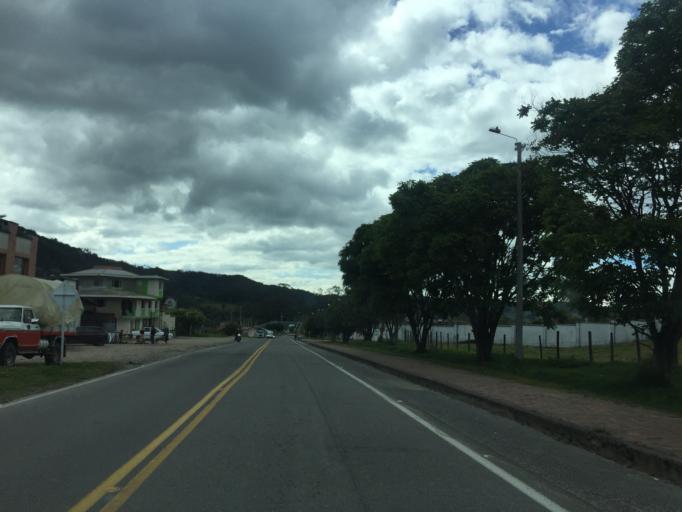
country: CO
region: Boyaca
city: Arcabuco
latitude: 5.7565
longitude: -73.4371
